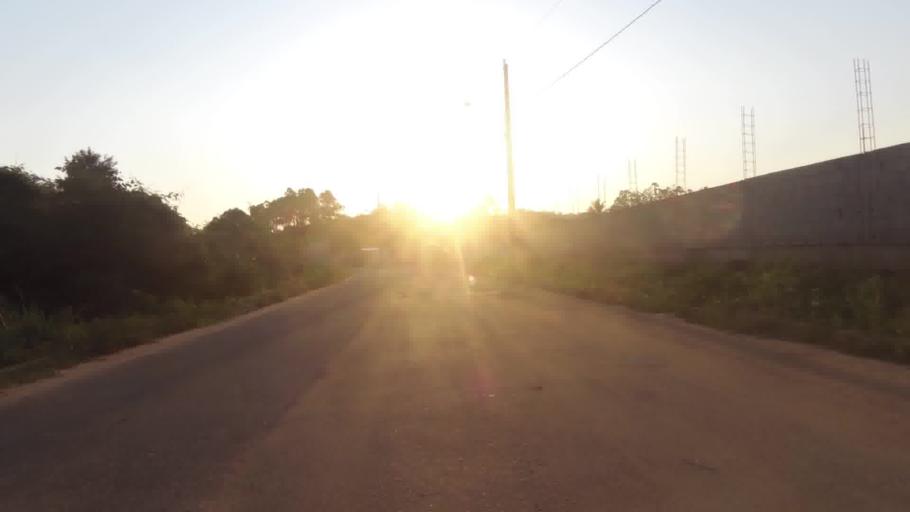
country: BR
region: Espirito Santo
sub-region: Piuma
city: Piuma
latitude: -20.8295
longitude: -40.7216
